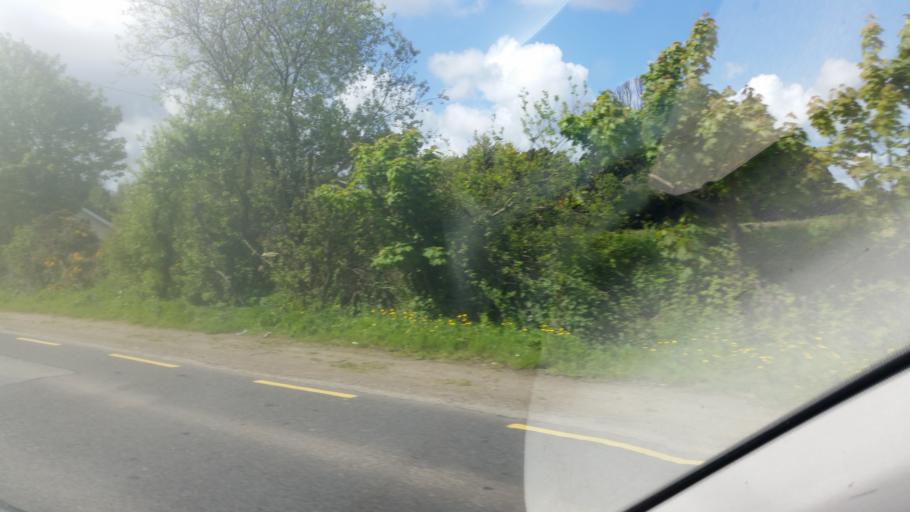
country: IE
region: Leinster
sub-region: Loch Garman
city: Loch Garman
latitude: 52.3506
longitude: -6.4552
